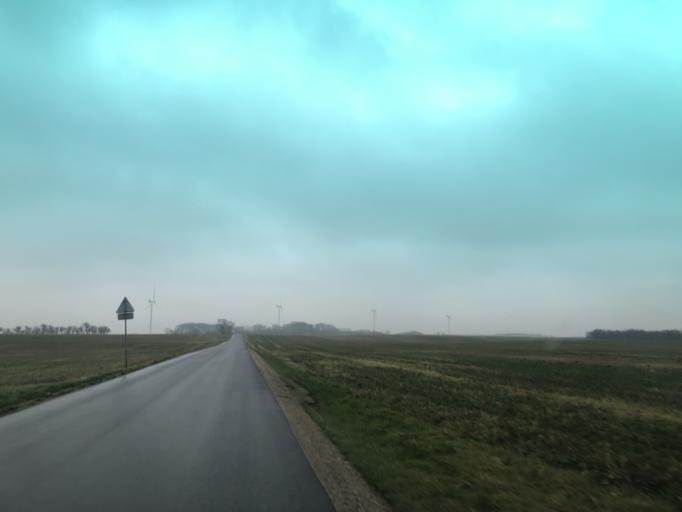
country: DK
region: Central Jutland
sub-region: Struer Kommune
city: Struer
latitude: 56.4338
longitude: 8.5852
